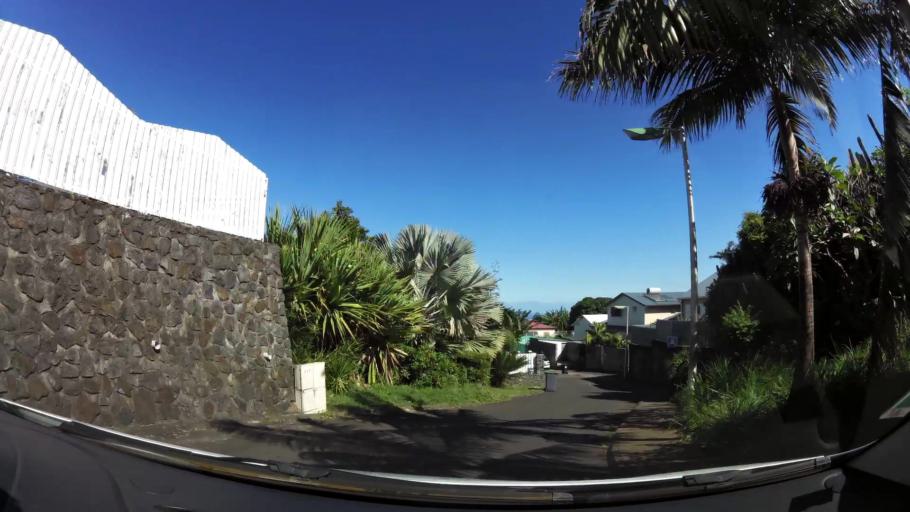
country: RE
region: Reunion
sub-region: Reunion
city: Le Tampon
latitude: -21.2769
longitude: 55.5081
